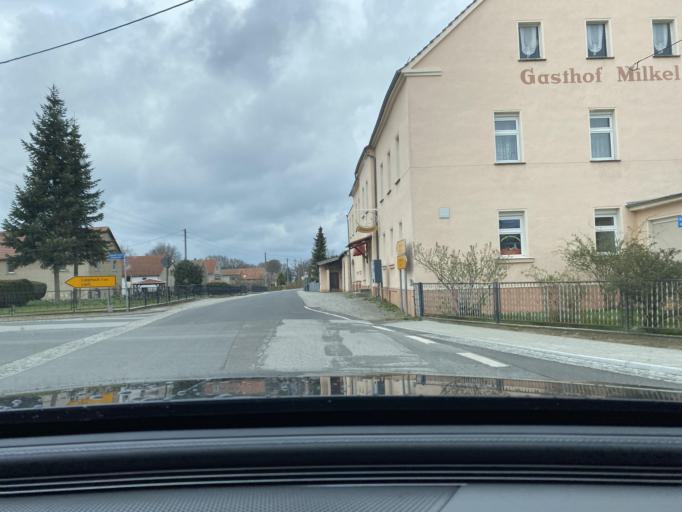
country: DE
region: Saxony
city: Grossdubrau
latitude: 51.2985
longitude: 14.4547
